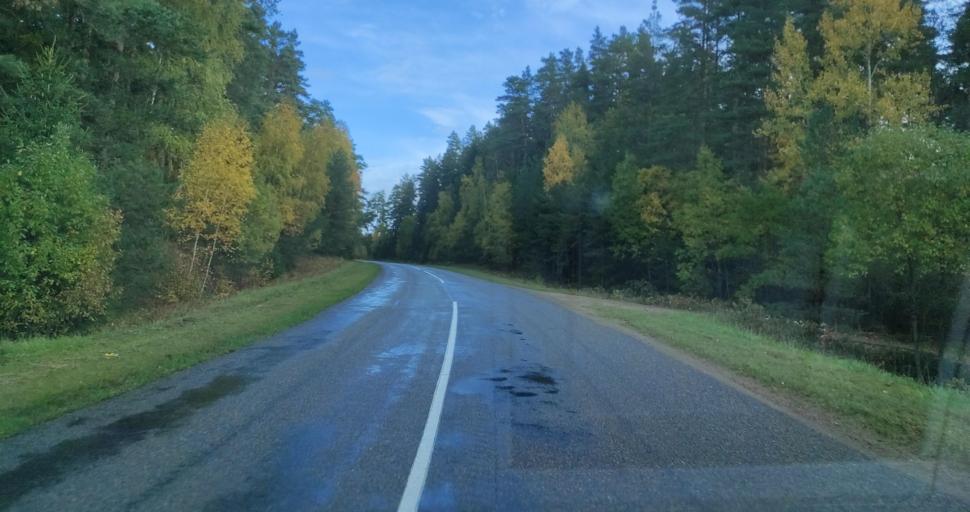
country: LV
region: Skrunda
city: Skrunda
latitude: 56.6331
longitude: 22.0027
